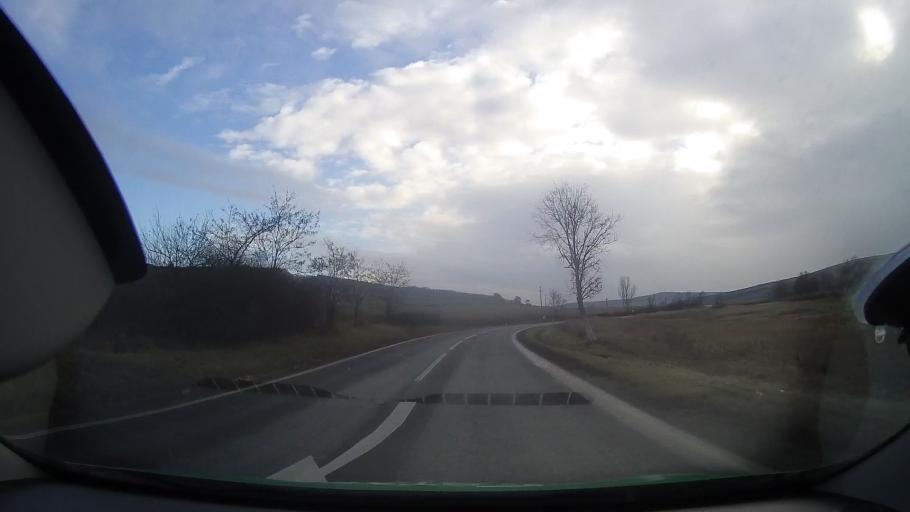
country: RO
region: Mures
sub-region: Comuna Cucerdea
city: Cucerdea
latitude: 46.3824
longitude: 24.2554
